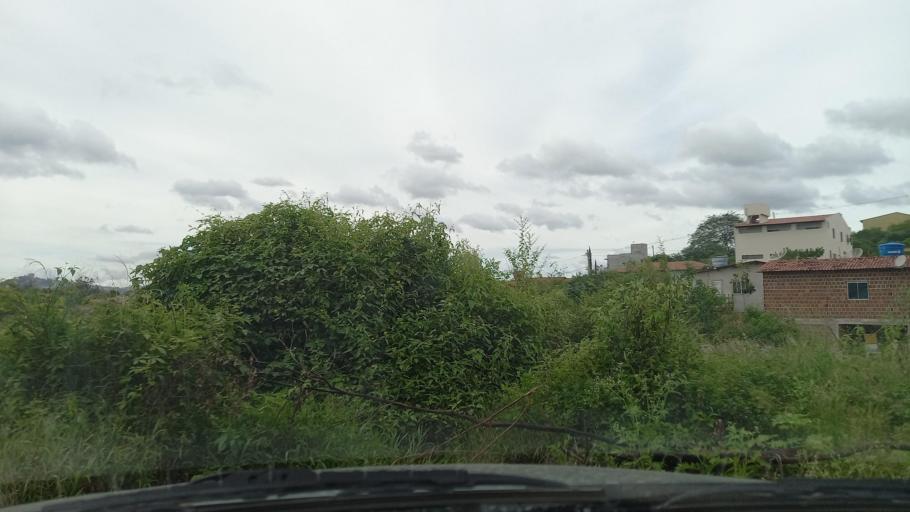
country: BR
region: Pernambuco
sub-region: Gravata
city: Gravata
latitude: -8.2144
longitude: -35.6016
